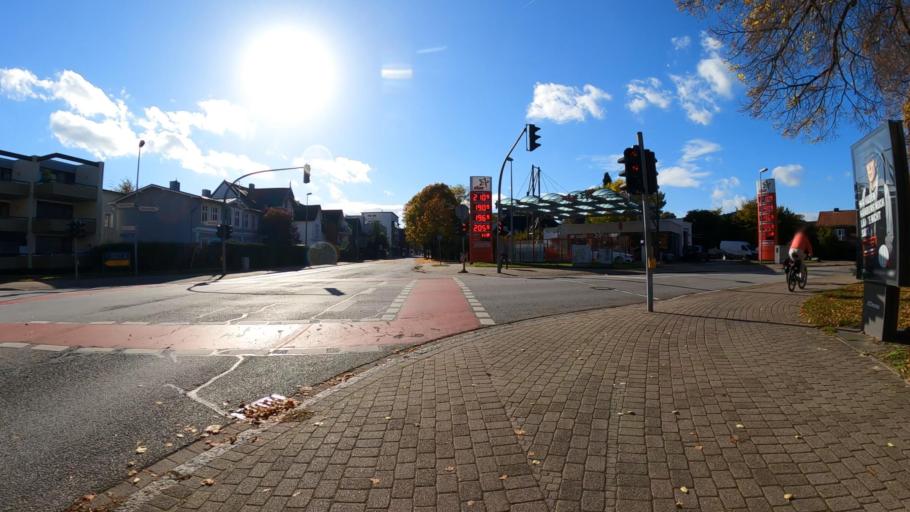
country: DE
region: Schleswig-Holstein
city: Ahrensburg
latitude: 53.6759
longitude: 10.2368
